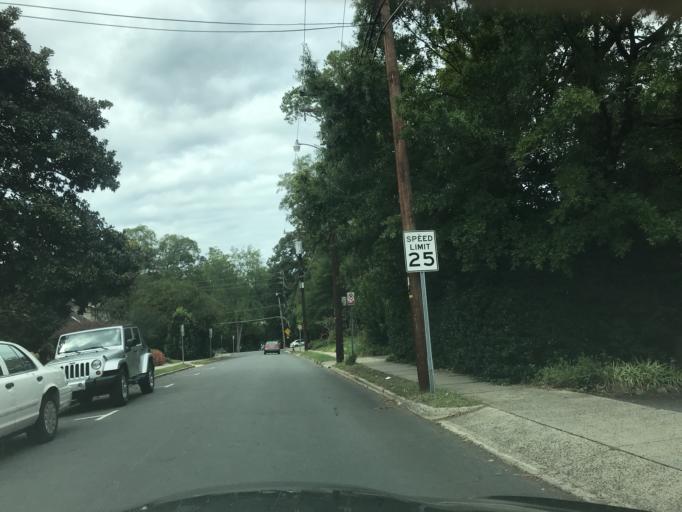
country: US
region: North Carolina
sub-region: Orange County
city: Chapel Hill
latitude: 35.9155
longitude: -79.0536
